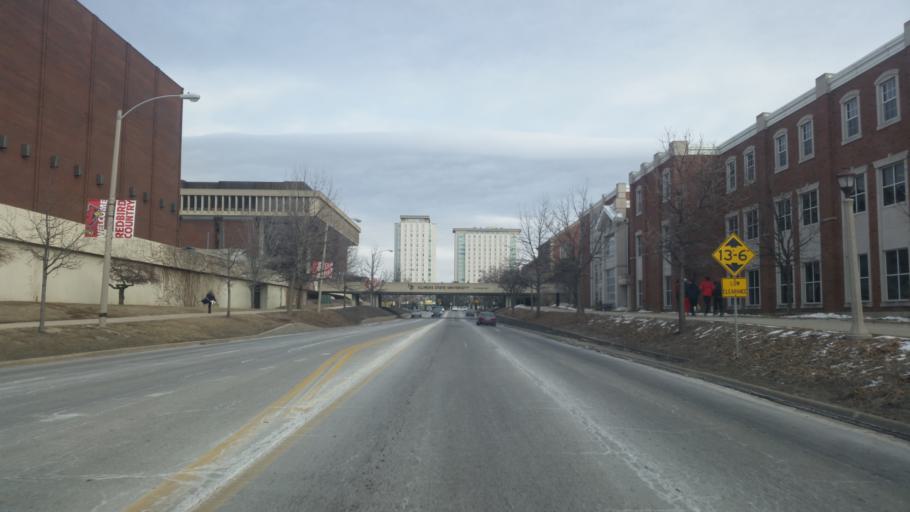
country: US
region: Illinois
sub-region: McLean County
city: Normal
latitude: 40.5108
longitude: -88.9930
